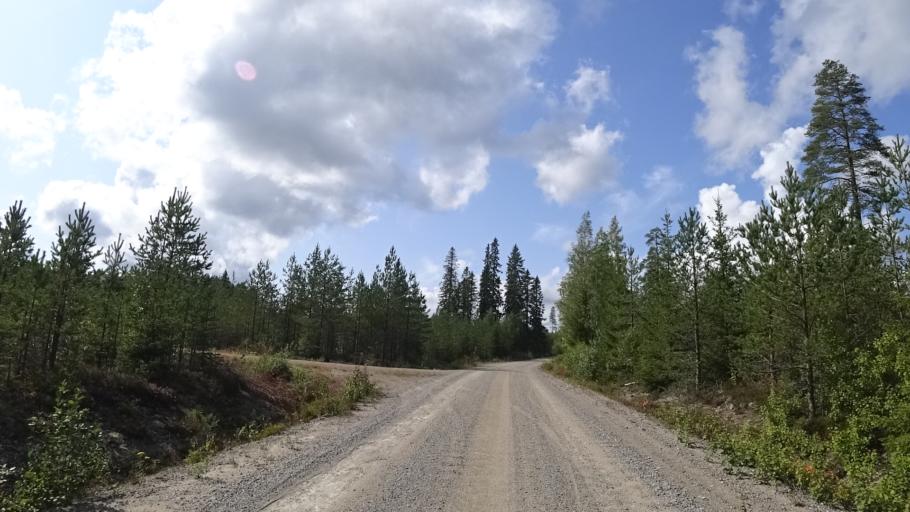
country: FI
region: North Karelia
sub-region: Joensuu
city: Ilomantsi
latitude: 62.9268
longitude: 31.3808
